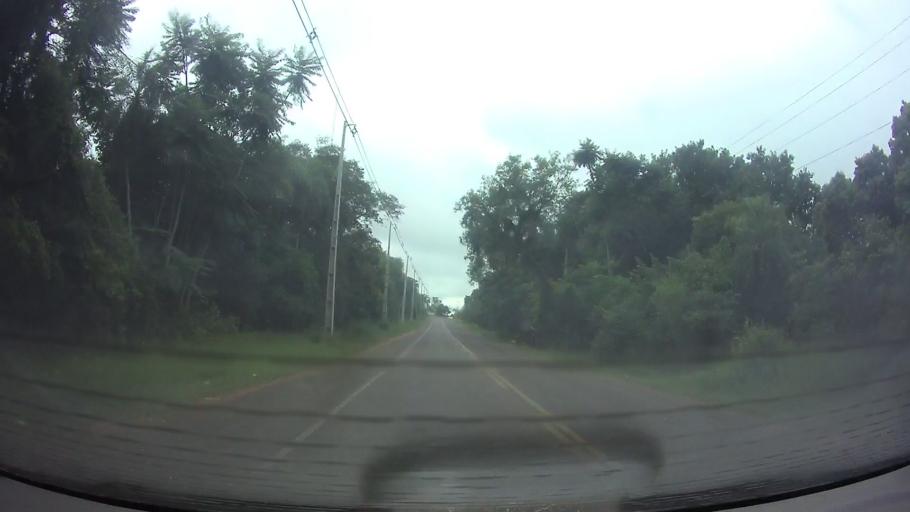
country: PY
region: Cordillera
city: Altos
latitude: -25.2775
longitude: -57.2611
